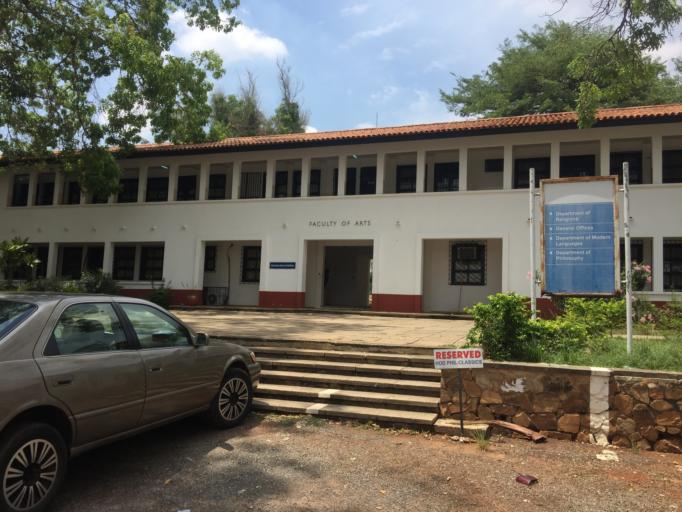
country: GH
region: Greater Accra
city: Medina Estates
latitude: 5.6508
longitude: -0.1884
